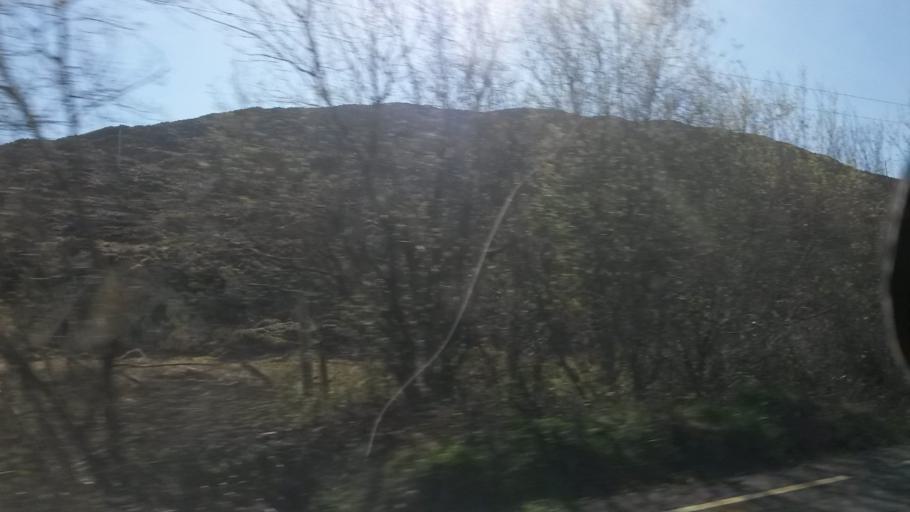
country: IE
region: Munster
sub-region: Ciarrai
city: Cill Airne
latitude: 51.9337
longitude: -9.3827
